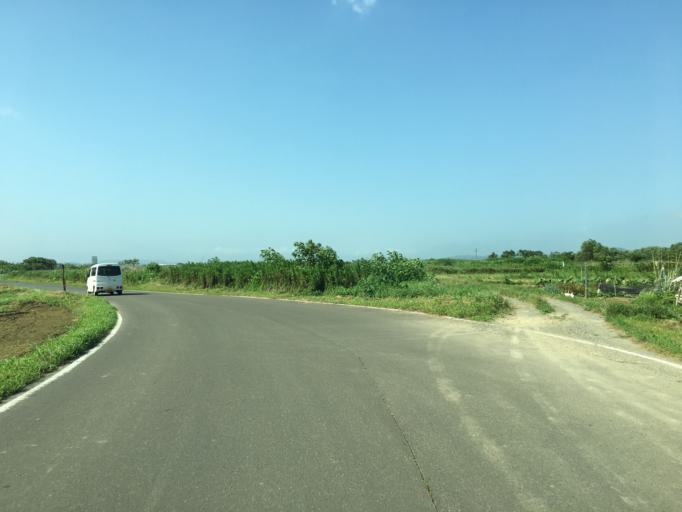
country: JP
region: Miyagi
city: Kakuda
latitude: 37.9619
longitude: 140.7901
